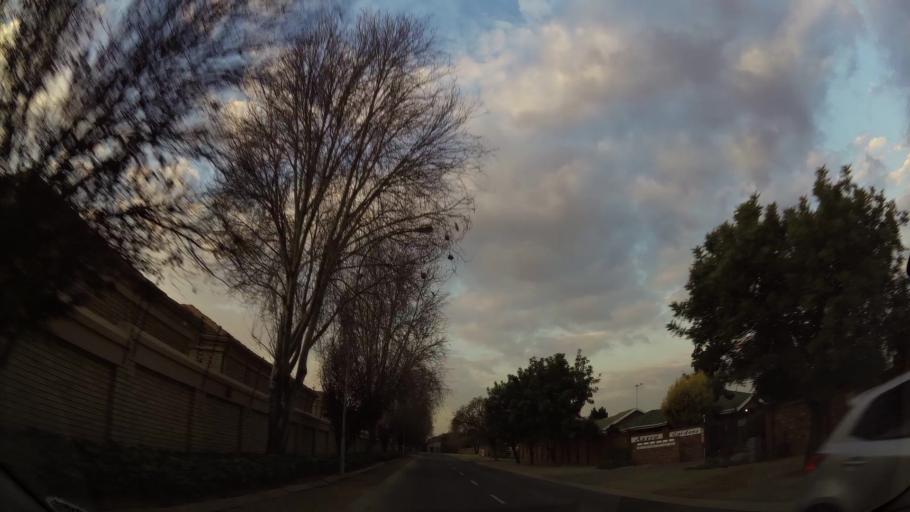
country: ZA
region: Gauteng
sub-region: Ekurhuleni Metropolitan Municipality
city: Benoni
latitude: -26.1699
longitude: 28.3080
